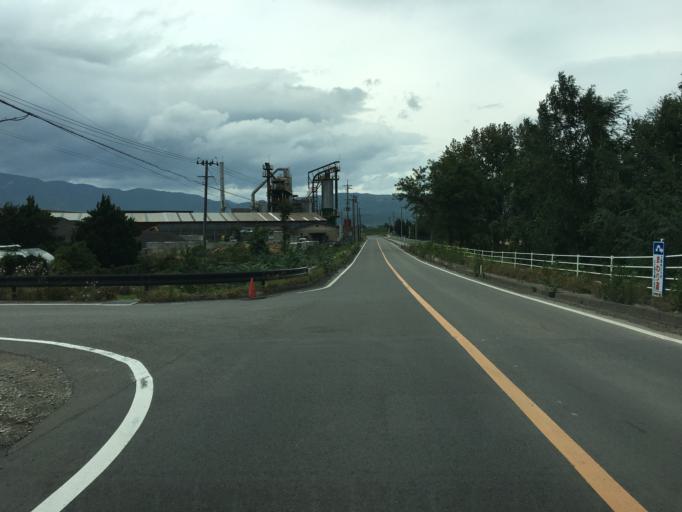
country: JP
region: Fukushima
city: Hobaramachi
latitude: 37.8393
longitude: 140.5584
